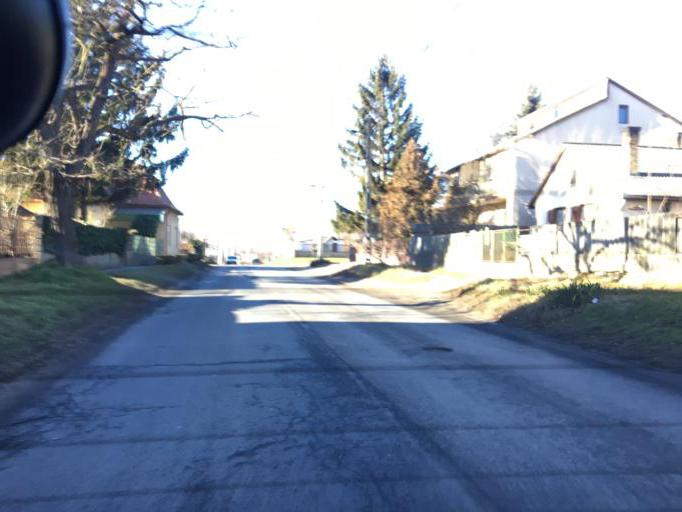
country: HU
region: Pest
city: Kiskunlachaza
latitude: 47.1729
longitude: 18.9950
